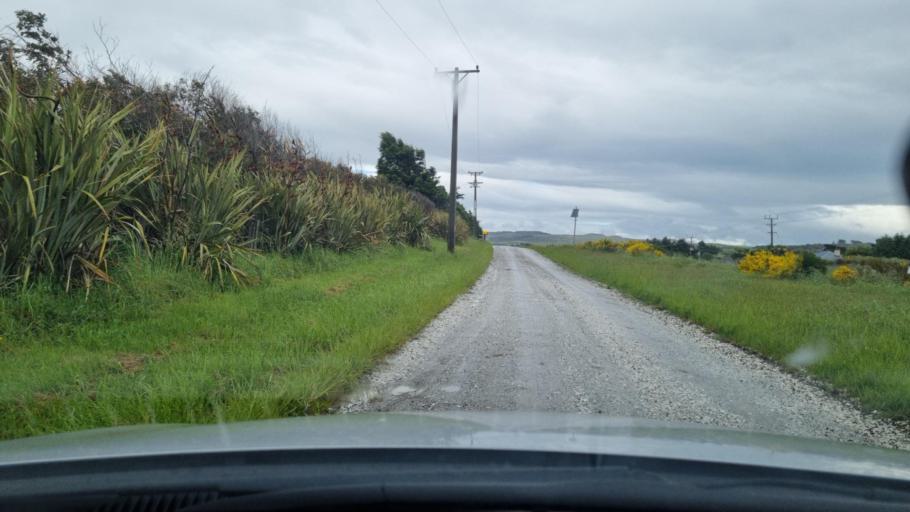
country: NZ
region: Southland
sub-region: Invercargill City
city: Bluff
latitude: -46.5438
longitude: 168.3019
